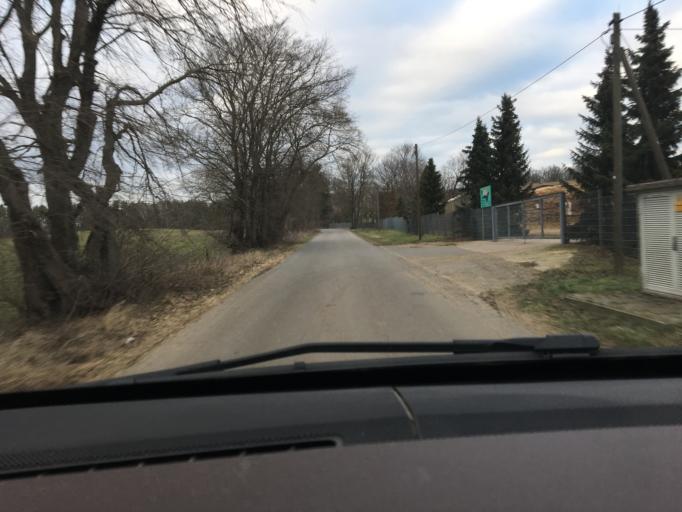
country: DE
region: Brandenburg
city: Marienwerder
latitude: 52.8622
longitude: 13.5097
